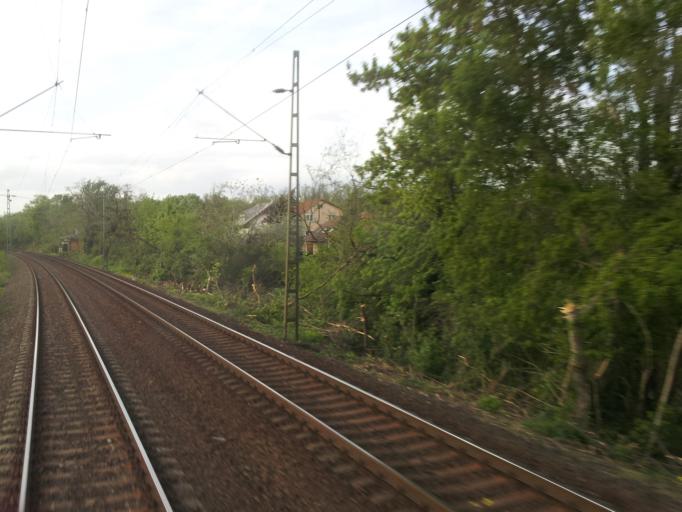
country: HU
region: Budapest
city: Budapest XVI. keruelet
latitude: 47.5092
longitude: 19.1555
